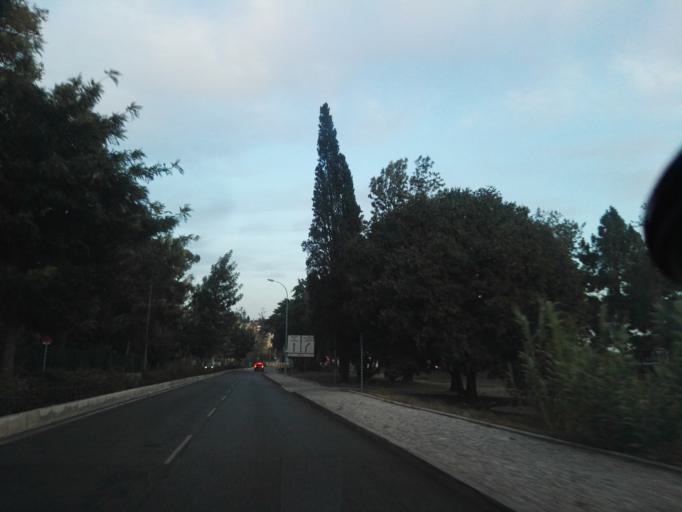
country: PT
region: Lisbon
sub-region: Oeiras
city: Linda-a-Velha
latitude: 38.7023
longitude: -9.2552
